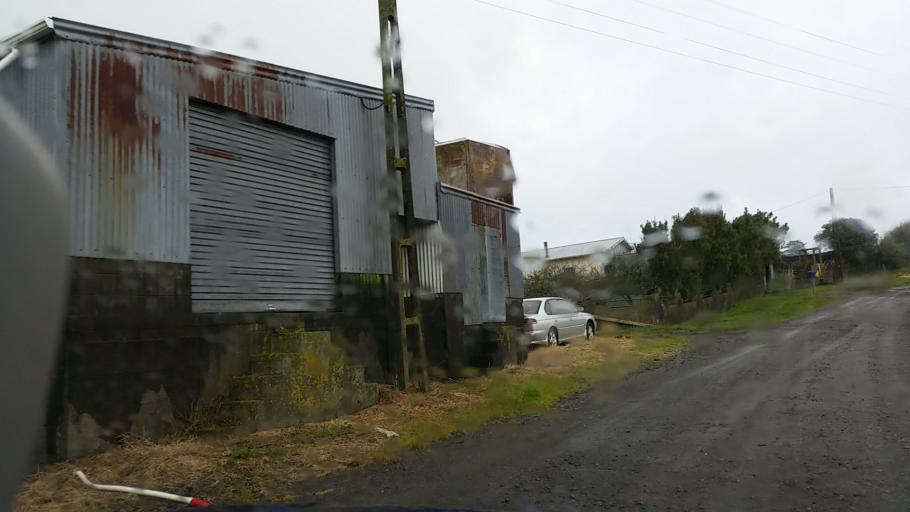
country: NZ
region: Taranaki
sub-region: South Taranaki District
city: Eltham
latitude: -39.2539
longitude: 174.2832
